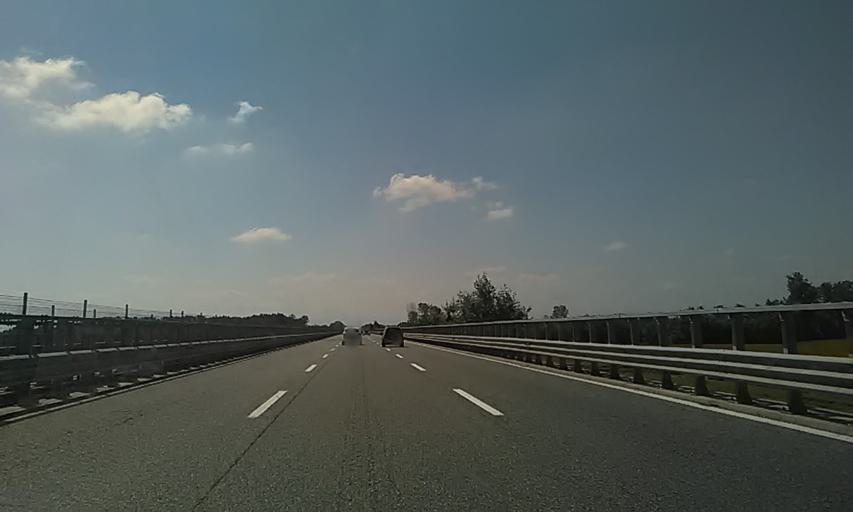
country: IT
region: Piedmont
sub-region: Provincia di Alessandria
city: Castellazzo Bormida
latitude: 44.8680
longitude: 8.5770
